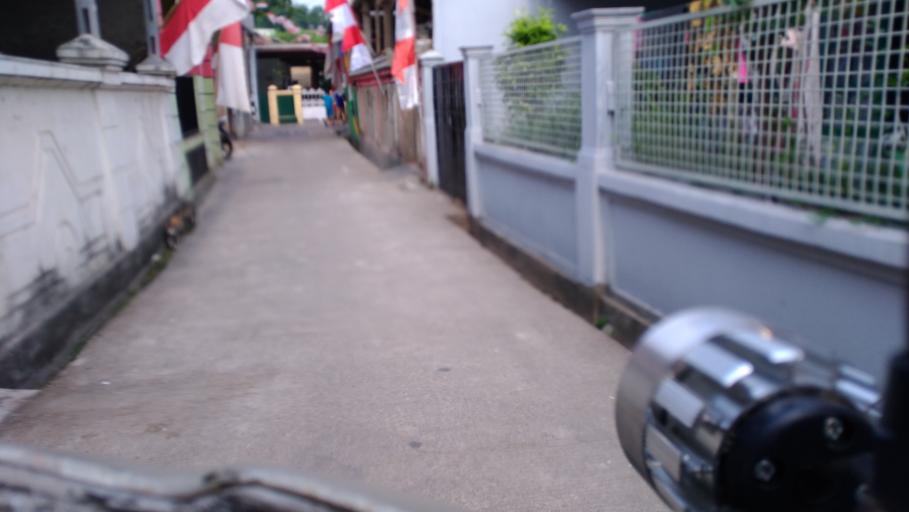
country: ID
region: West Java
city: Depok
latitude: -6.3560
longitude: 106.8733
